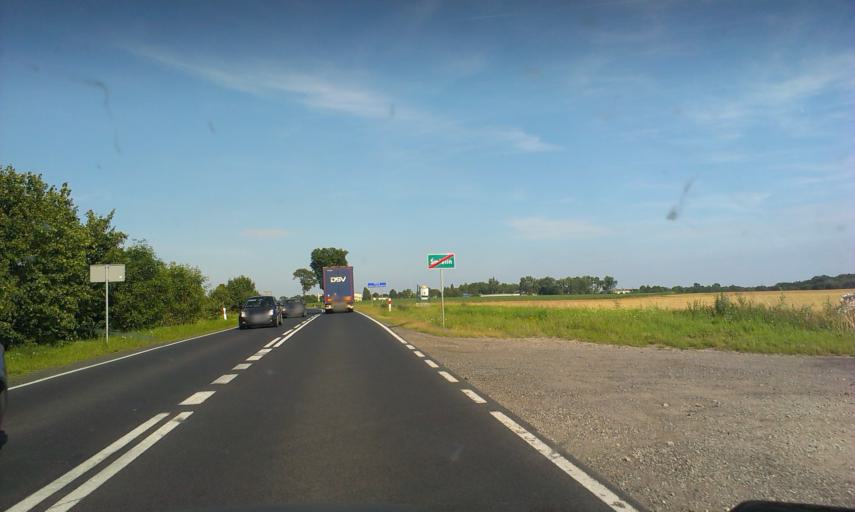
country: PL
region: Kujawsko-Pomorskie
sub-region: Powiat nakielski
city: Sadki
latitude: 53.1485
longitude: 17.5147
